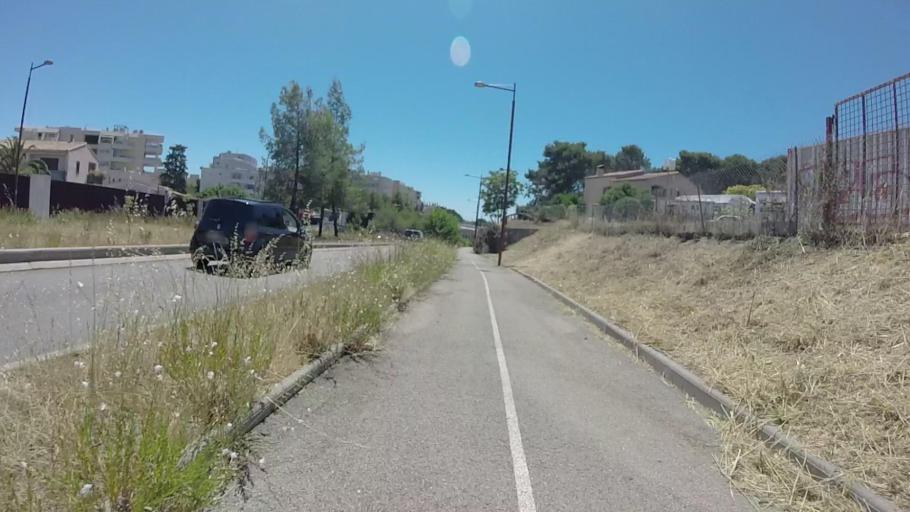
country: FR
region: Provence-Alpes-Cote d'Azur
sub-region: Departement des Alpes-Maritimes
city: Biot
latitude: 43.5948
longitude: 7.0907
